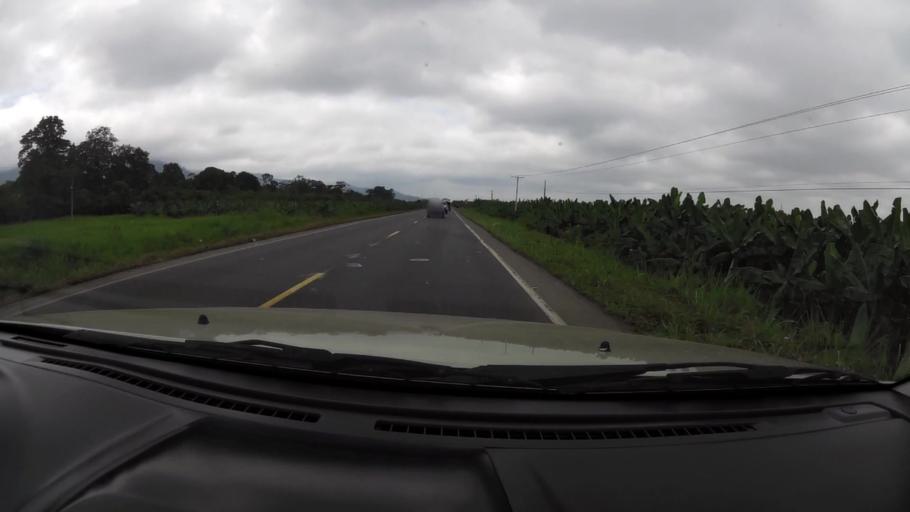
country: EC
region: Guayas
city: Naranjal
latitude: -2.7314
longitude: -79.6764
